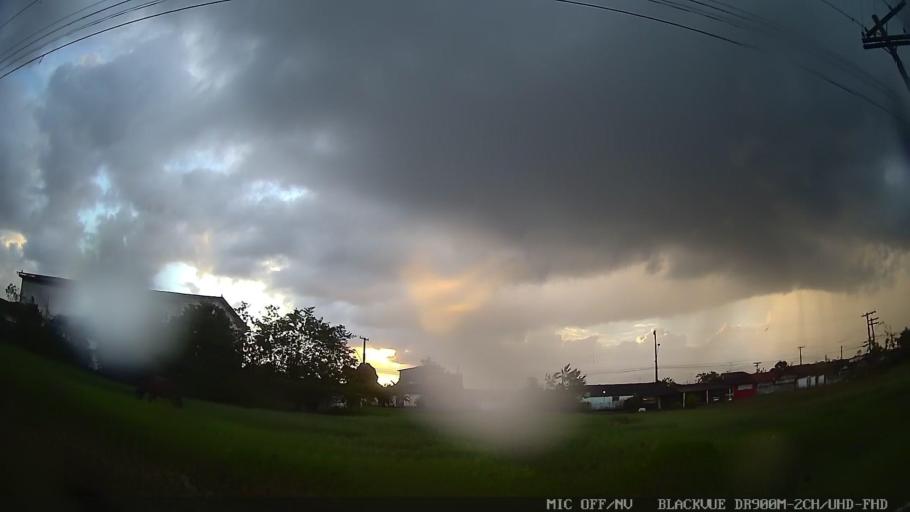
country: BR
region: Sao Paulo
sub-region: Itanhaem
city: Itanhaem
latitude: -24.1530
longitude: -46.7796
